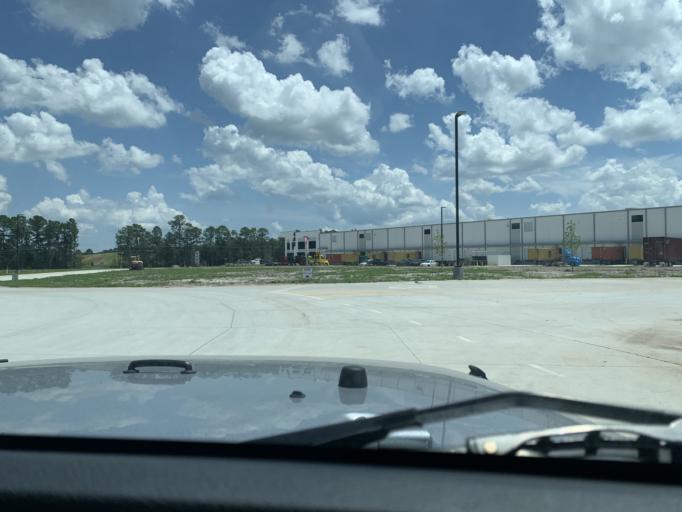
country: US
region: Georgia
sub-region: Chatham County
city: Bloomingdale
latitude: 32.1178
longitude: -81.2779
